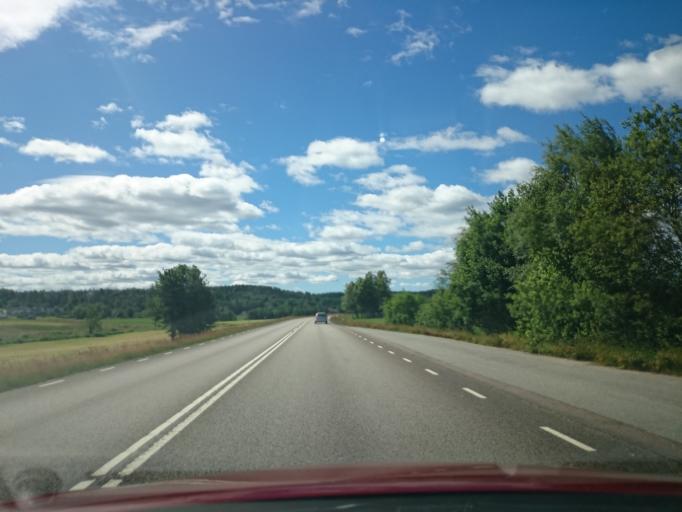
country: SE
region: Vaestra Goetaland
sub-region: Lerums Kommun
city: Olstorp
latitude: 57.8311
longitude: 12.2545
